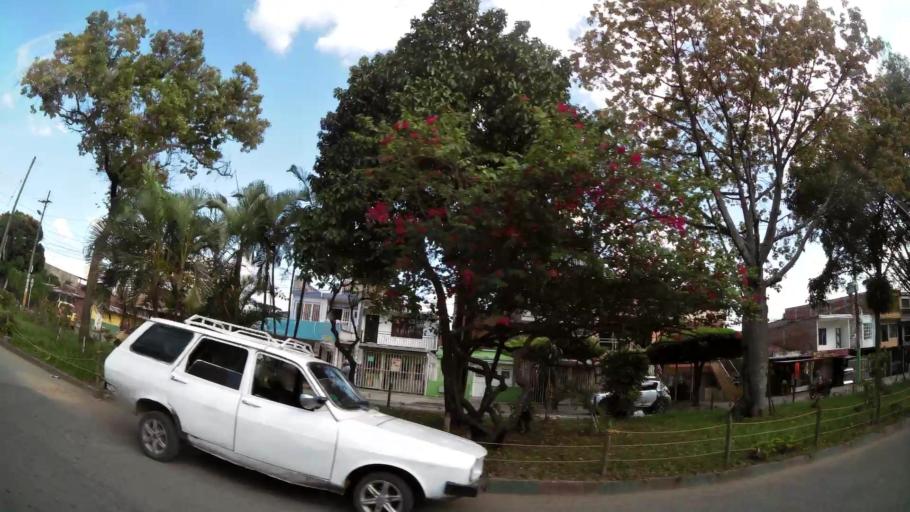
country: CO
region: Valle del Cauca
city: Cali
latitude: 3.4220
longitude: -76.4982
